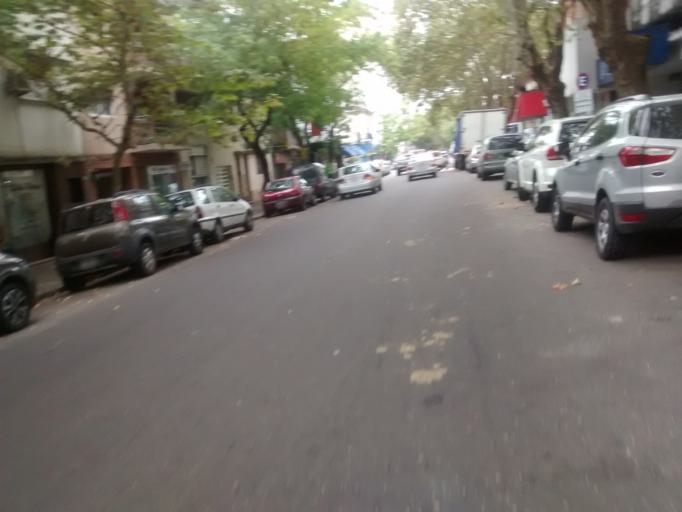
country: AR
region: Buenos Aires
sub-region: Partido de La Plata
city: La Plata
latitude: -34.9225
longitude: -57.9493
